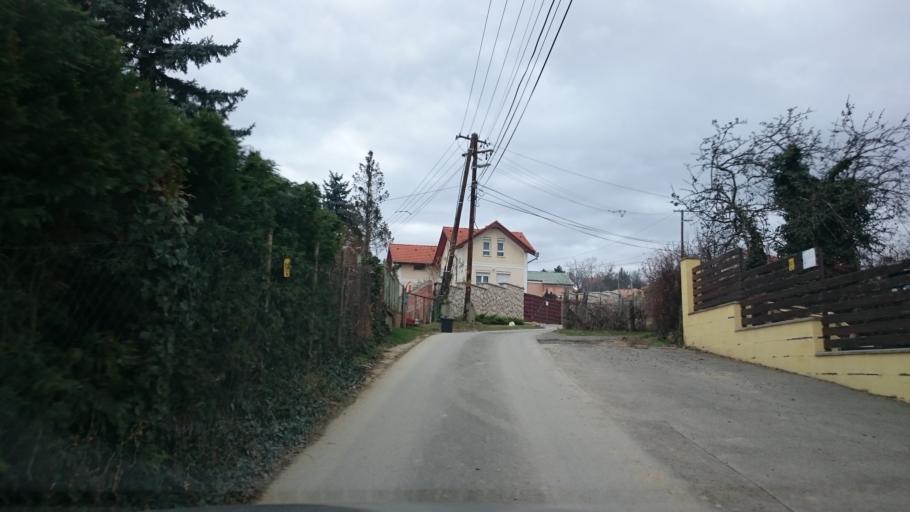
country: HU
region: Baranya
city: Pellerd
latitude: 46.0706
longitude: 18.1808
